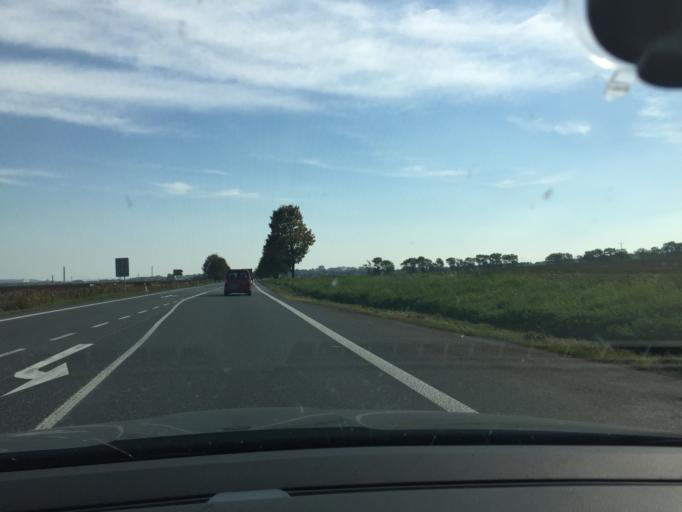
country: CZ
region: Central Bohemia
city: Velim
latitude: 50.0355
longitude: 15.1498
